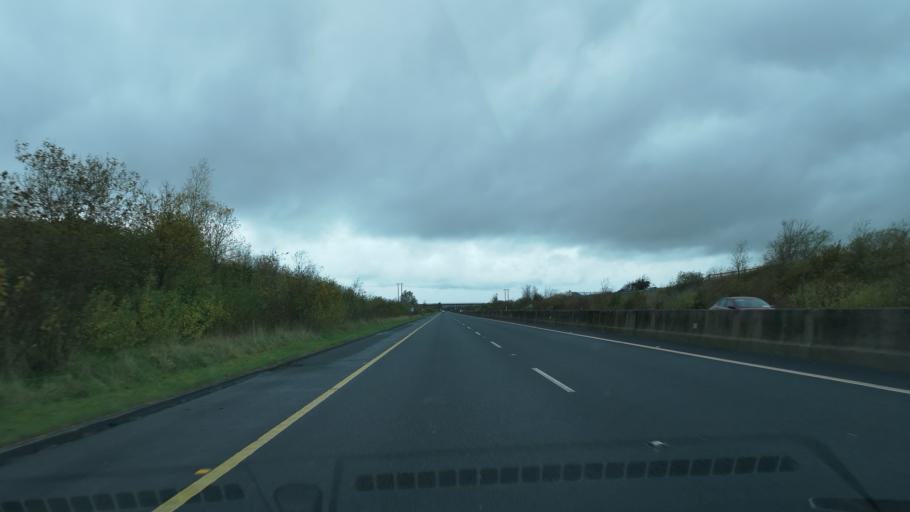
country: IE
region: Connaught
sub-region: County Galway
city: Athenry
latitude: 53.2746
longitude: -8.7064
